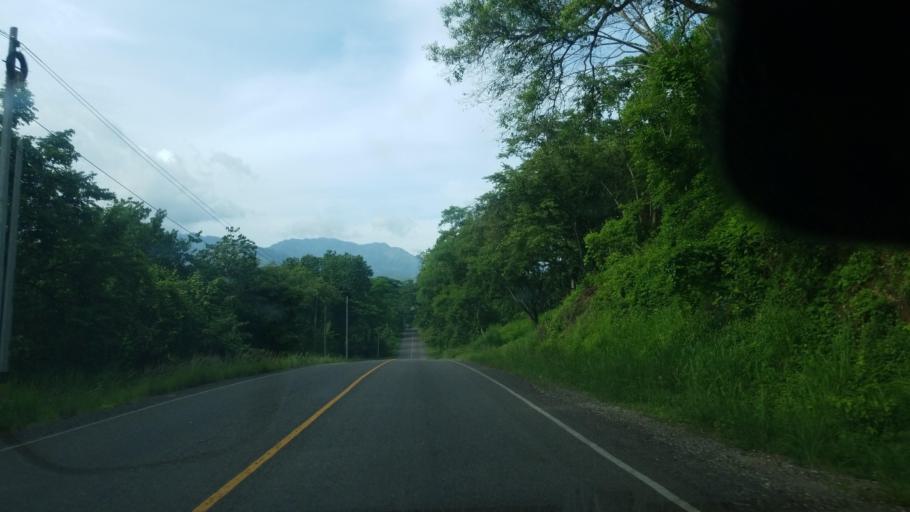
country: HN
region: Santa Barbara
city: Trinidad
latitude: 15.1321
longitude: -88.2499
